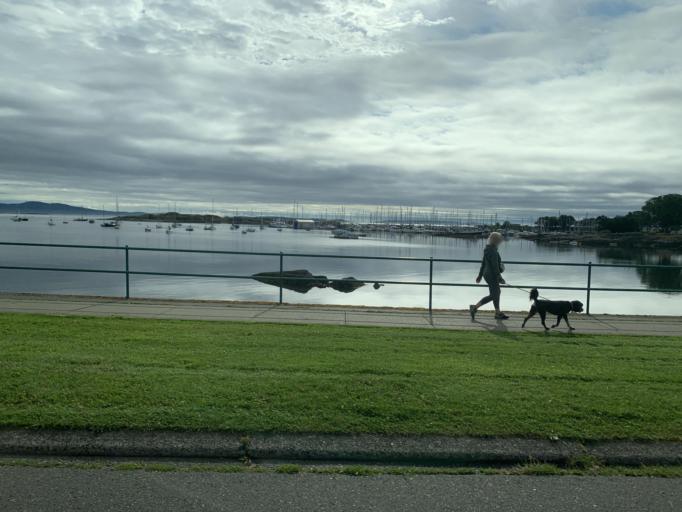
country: CA
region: British Columbia
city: Oak Bay
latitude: 48.4255
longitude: -123.3074
